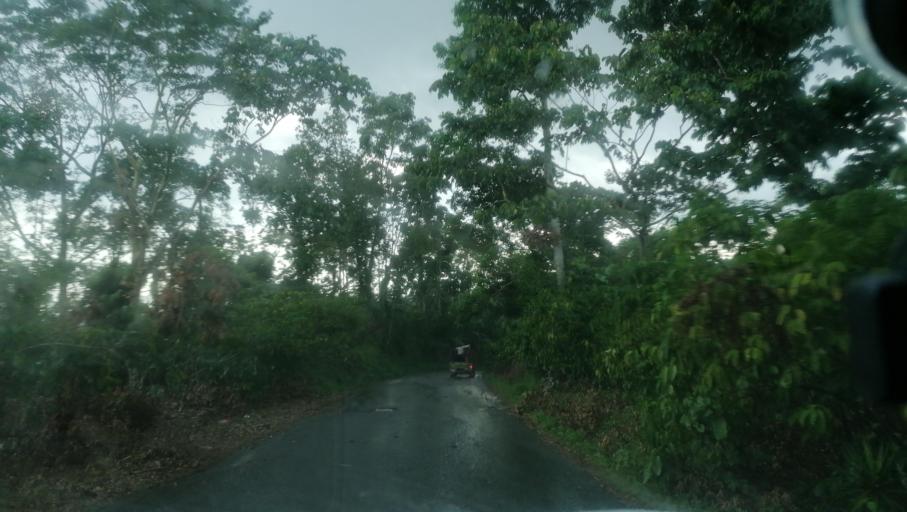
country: MX
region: Chiapas
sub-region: Cacahoatan
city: Benito Juarez
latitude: 15.0634
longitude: -92.1921
